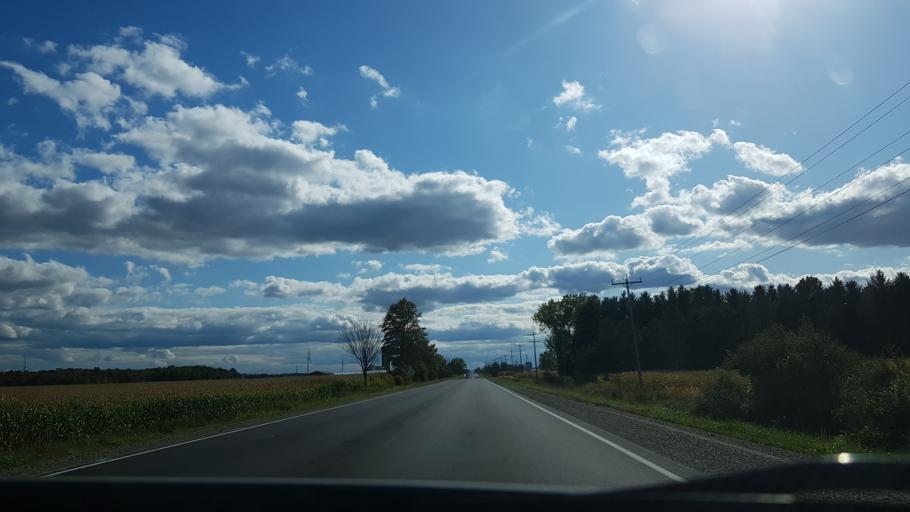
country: CA
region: Ontario
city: South Huron
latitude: 43.1472
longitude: -81.6629
